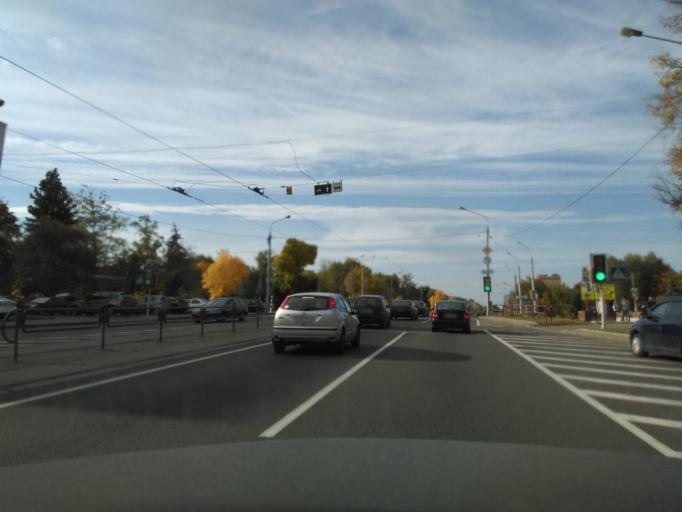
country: BY
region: Minsk
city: Minsk
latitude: 53.8901
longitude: 27.6145
